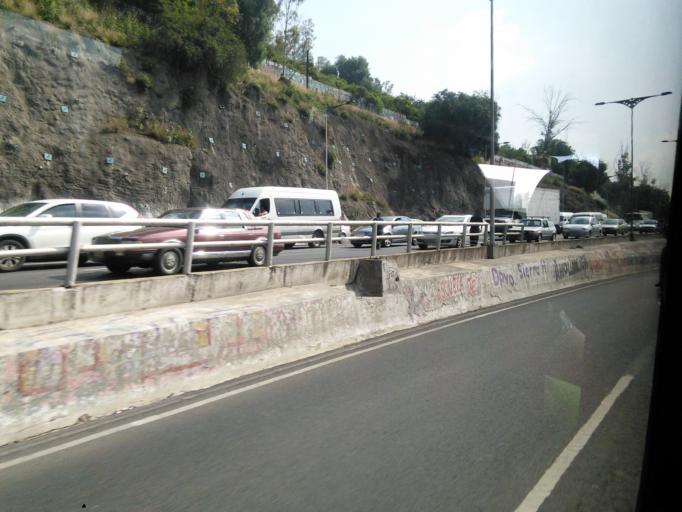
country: MX
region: Mexico City
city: Gustavo A. Madero
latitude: 19.5033
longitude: -99.1149
